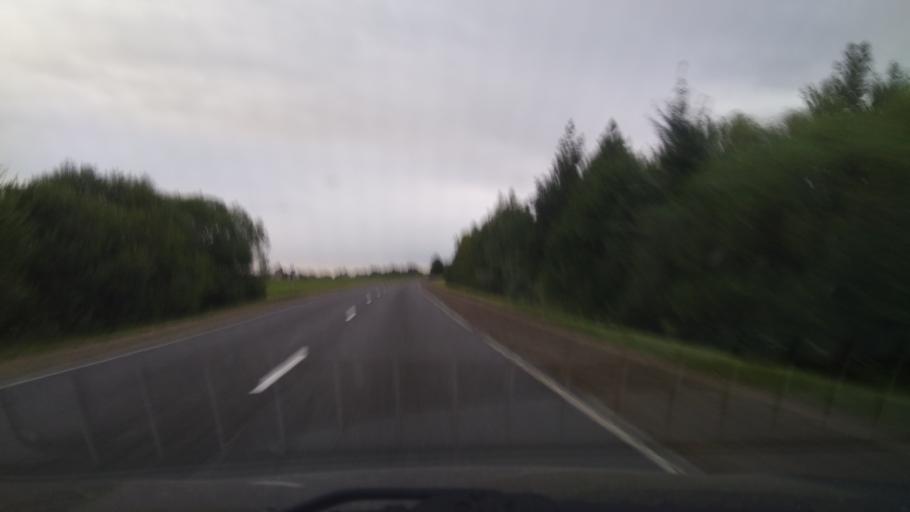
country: BY
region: Brest
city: Byaroza
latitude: 52.4469
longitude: 24.9721
